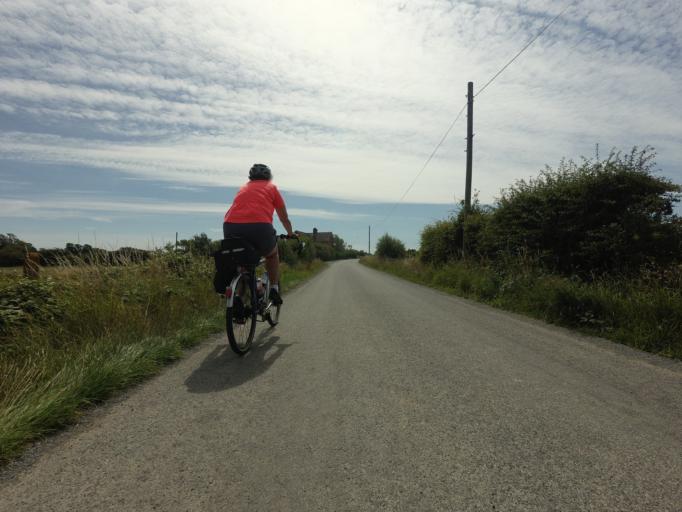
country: GB
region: England
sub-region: Kent
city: Stone
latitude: 51.0017
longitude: 0.8026
